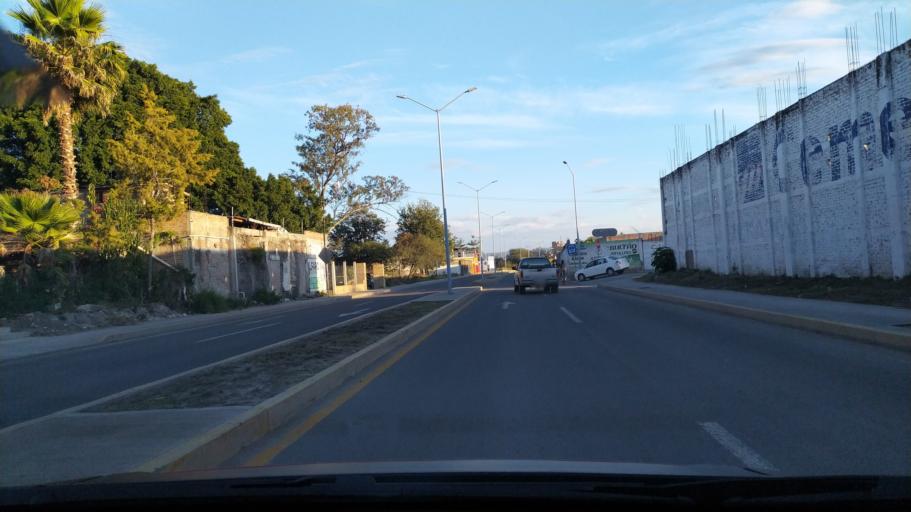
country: MX
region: Guanajuato
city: Ciudad Manuel Doblado
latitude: 20.7340
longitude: -101.9477
